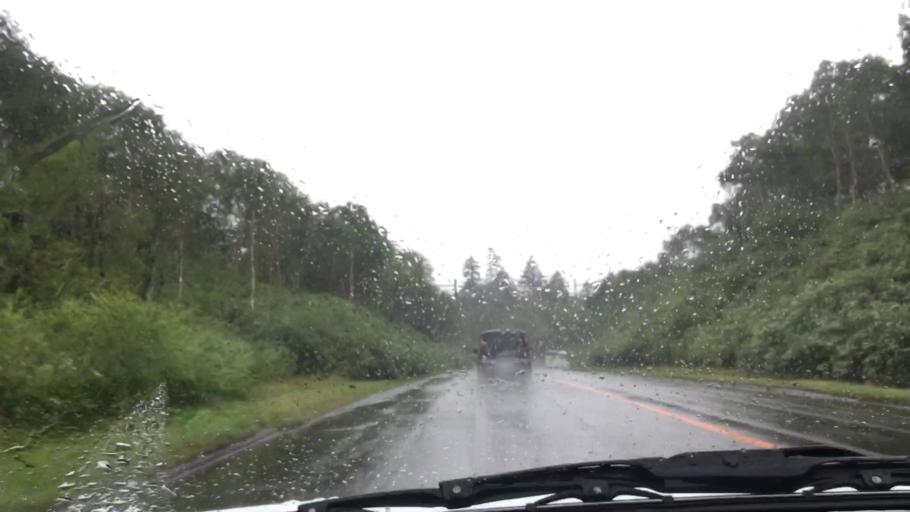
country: JP
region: Hokkaido
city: Sapporo
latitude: 42.8670
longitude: 141.1105
